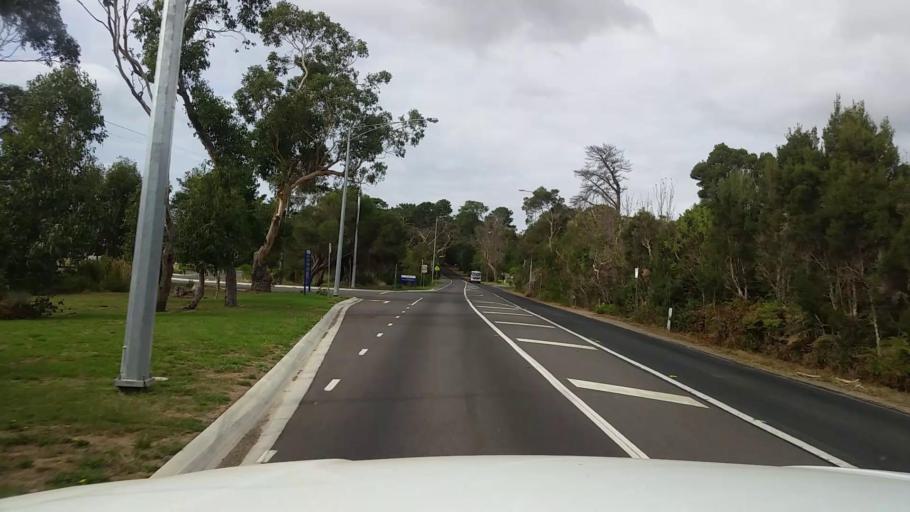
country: AU
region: Victoria
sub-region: Mornington Peninsula
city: Balnarring
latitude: -38.3625
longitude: 145.1156
